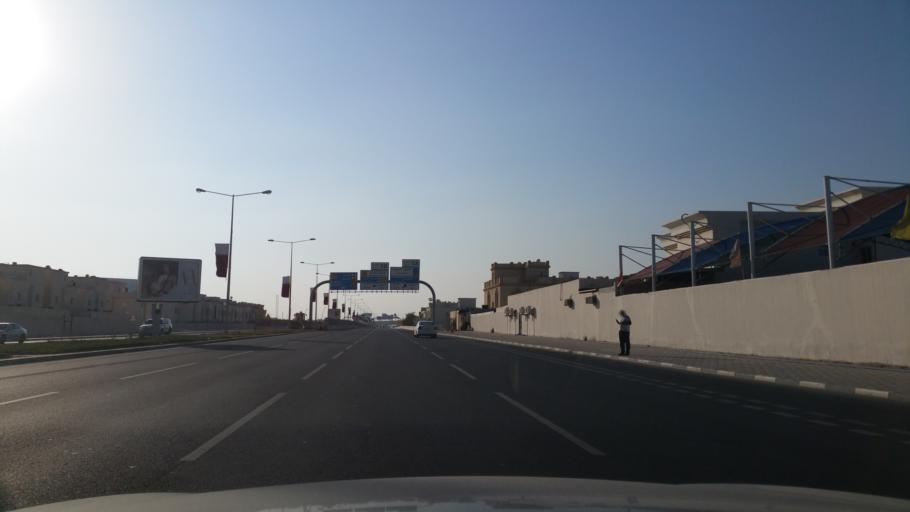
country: QA
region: Baladiyat ad Dawhah
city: Doha
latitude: 25.2388
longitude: 51.5383
